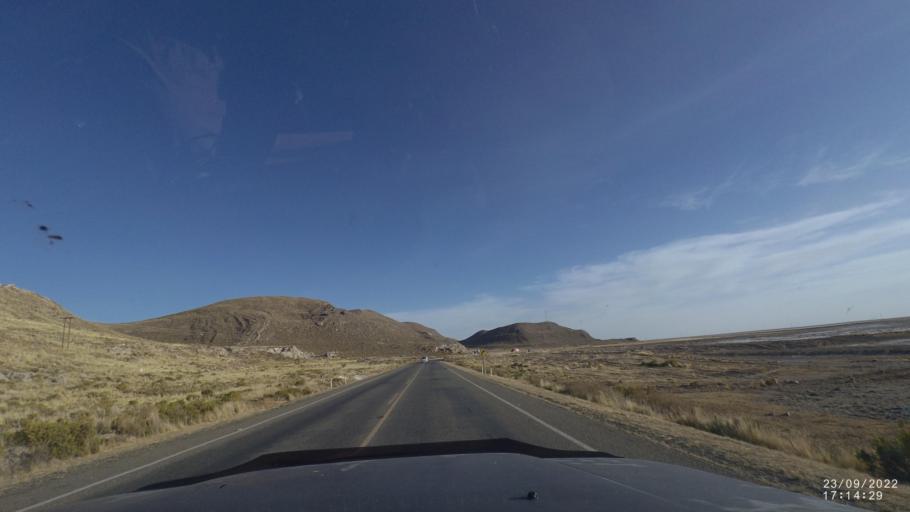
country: BO
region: Oruro
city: Challapata
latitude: -18.7224
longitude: -66.8668
